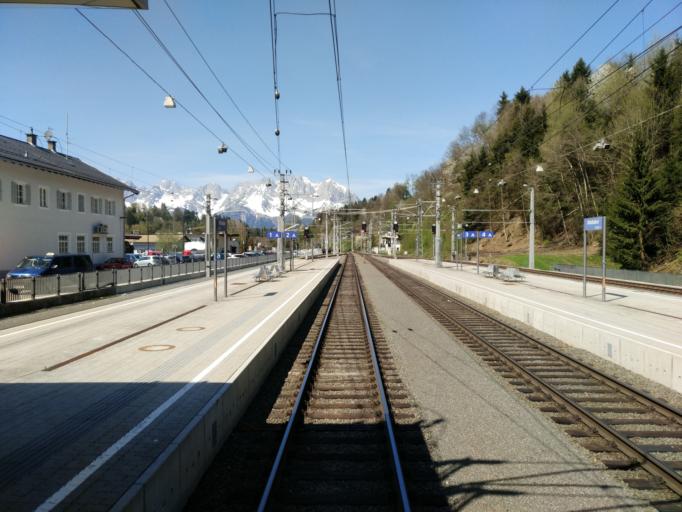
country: AT
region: Tyrol
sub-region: Politischer Bezirk Kitzbuhel
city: Kitzbuhel
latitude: 47.4545
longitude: 12.3910
